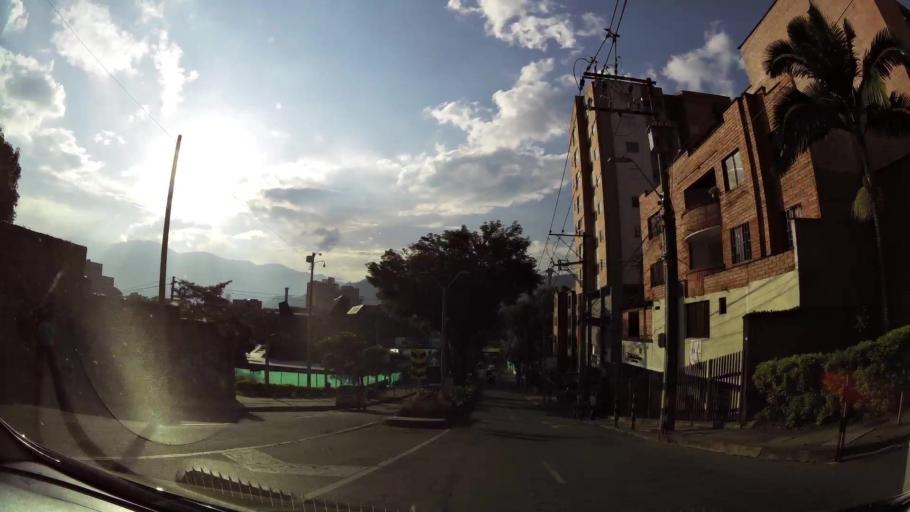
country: CO
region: Antioquia
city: Envigado
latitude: 6.1721
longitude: -75.5897
